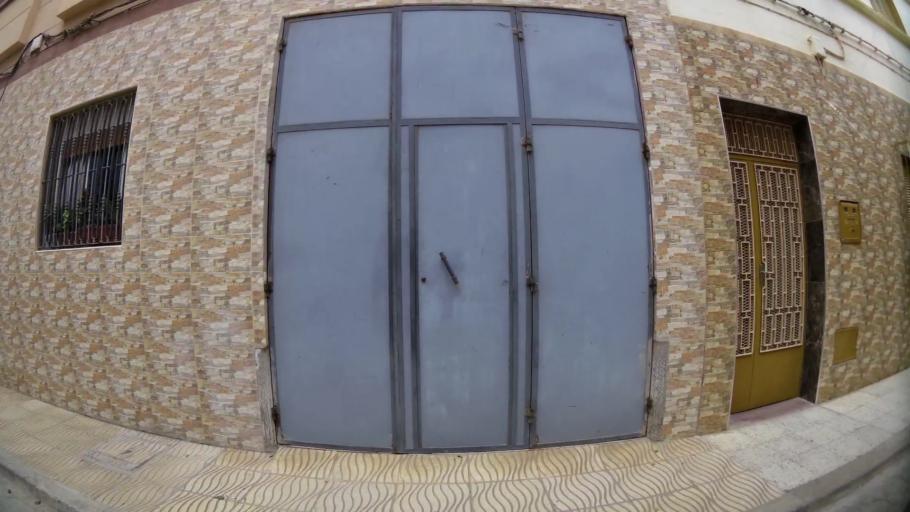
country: MA
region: Oriental
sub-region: Nador
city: Nador
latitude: 35.1705
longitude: -2.9261
